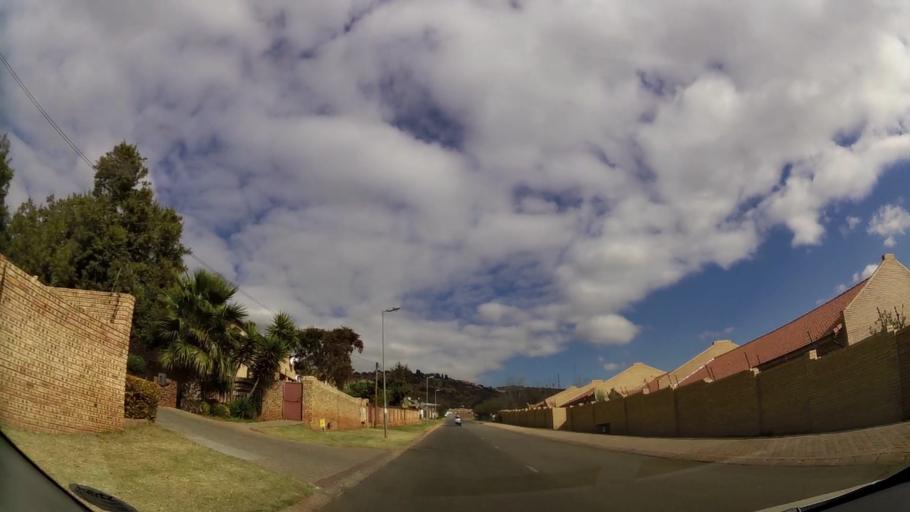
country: ZA
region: Gauteng
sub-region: City of Johannesburg Metropolitan Municipality
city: Roodepoort
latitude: -26.1031
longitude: 27.8733
